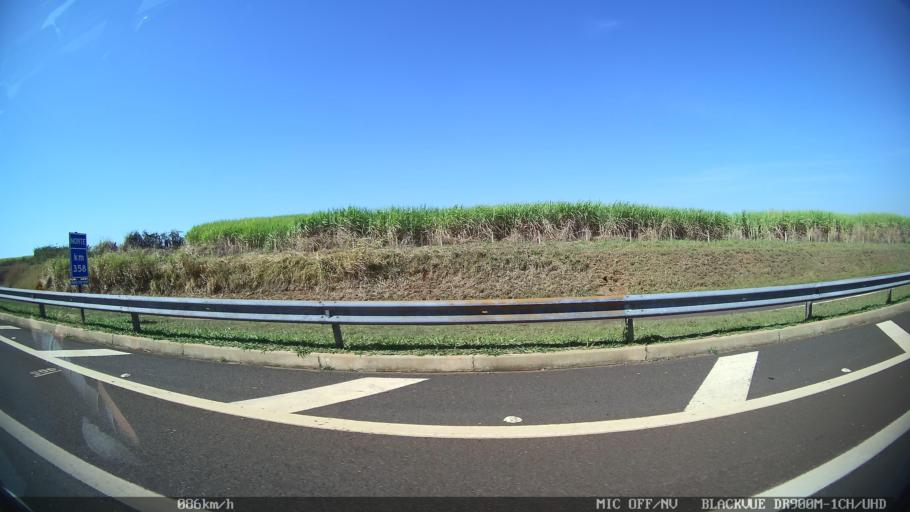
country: BR
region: Sao Paulo
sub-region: Batatais
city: Batatais
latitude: -20.8300
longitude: -47.5979
